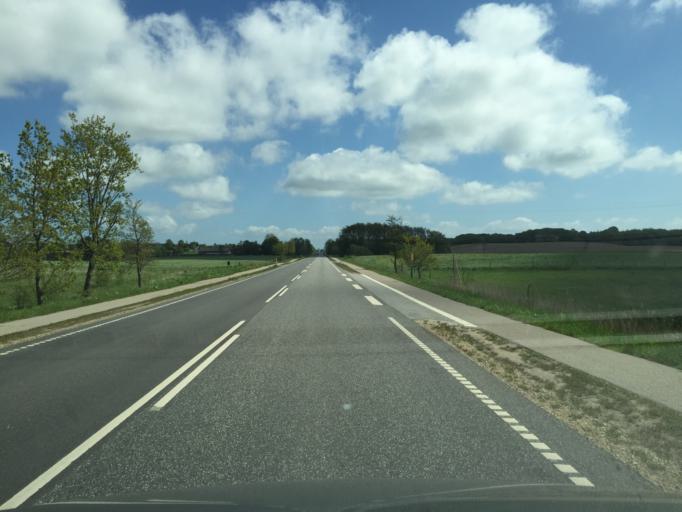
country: DK
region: Zealand
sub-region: Vordingborg Kommune
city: Nyrad
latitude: 54.9969
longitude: 12.0621
